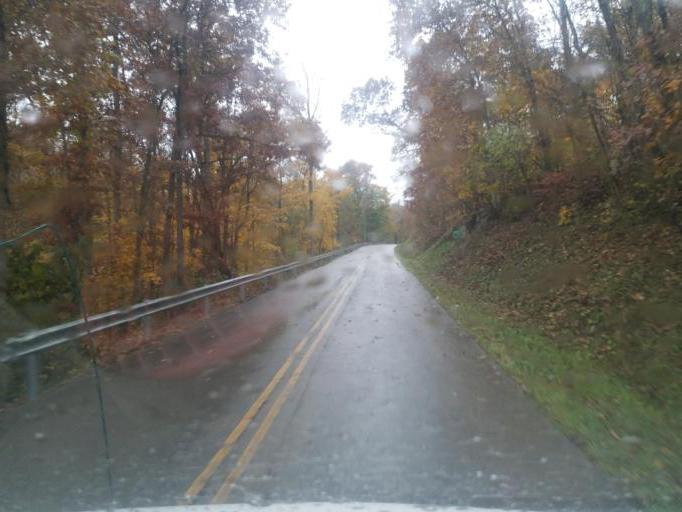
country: US
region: Ohio
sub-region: Washington County
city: Beverly
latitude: 39.4330
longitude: -81.6198
